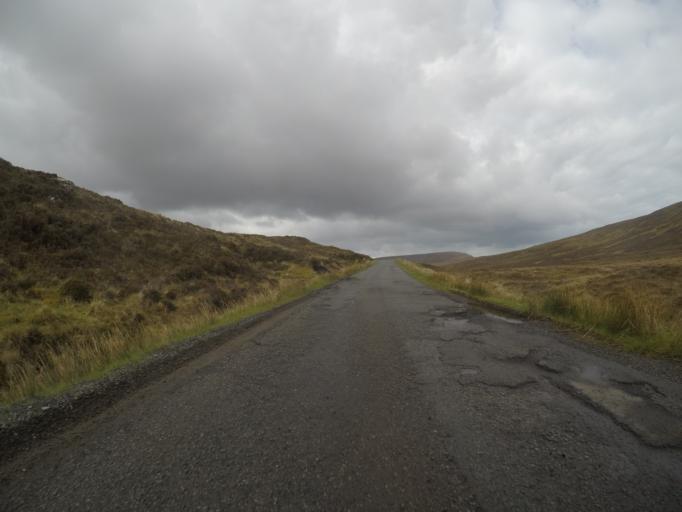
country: GB
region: Scotland
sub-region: Highland
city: Portree
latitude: 57.6256
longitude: -6.2961
